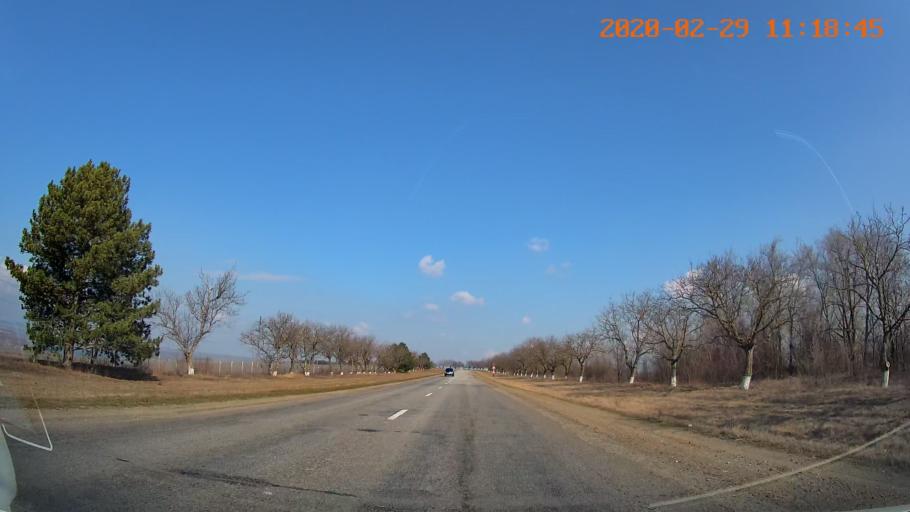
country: MD
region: Telenesti
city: Cocieri
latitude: 47.3394
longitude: 29.1749
